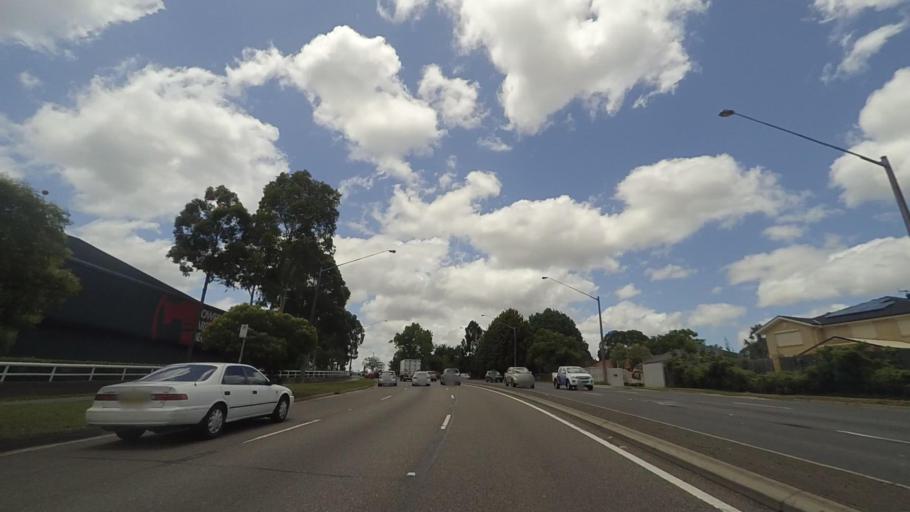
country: AU
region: New South Wales
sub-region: Hornsby Shire
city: Pennant Hills
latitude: -33.7297
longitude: 151.0830
